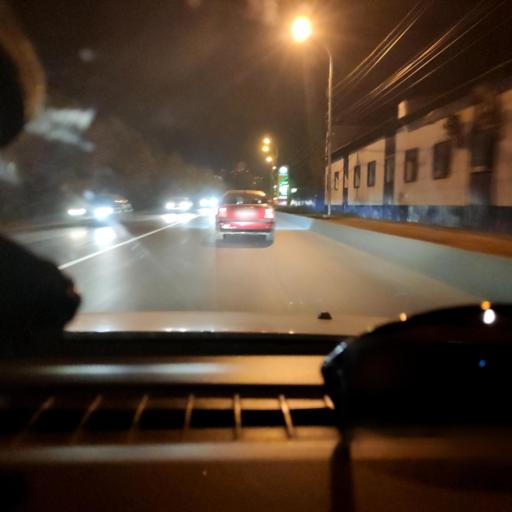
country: RU
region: Samara
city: Rozhdestveno
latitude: 53.1638
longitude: 50.0762
